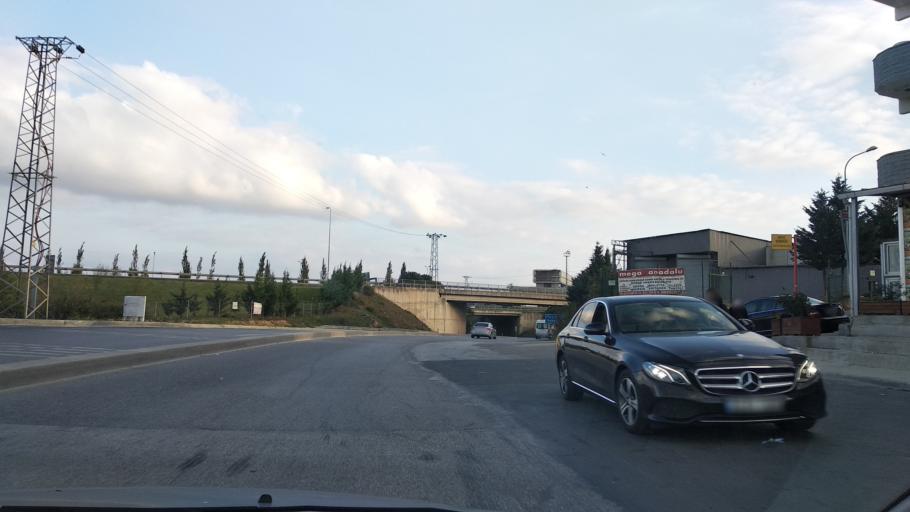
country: TR
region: Istanbul
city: Sultanbeyli
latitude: 40.9297
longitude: 29.3437
